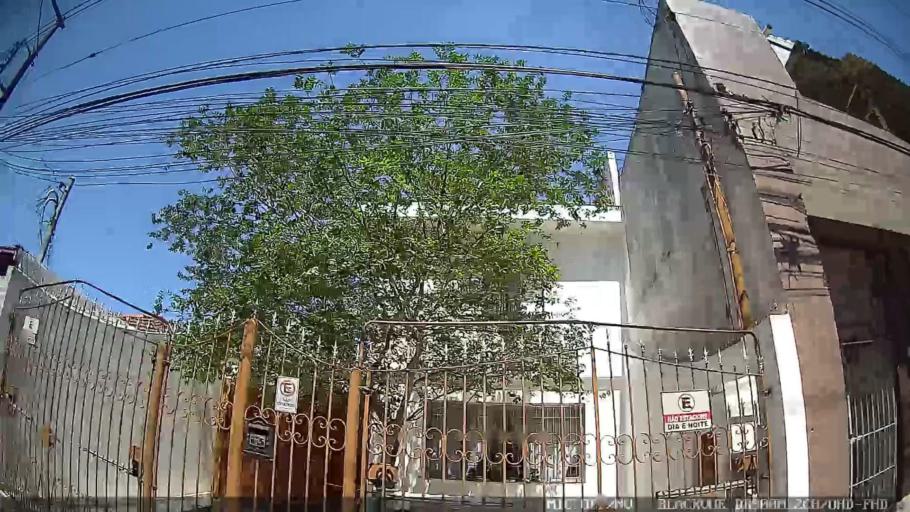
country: BR
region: Sao Paulo
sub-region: Sao Caetano Do Sul
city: Sao Caetano do Sul
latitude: -23.5895
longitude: -46.5331
